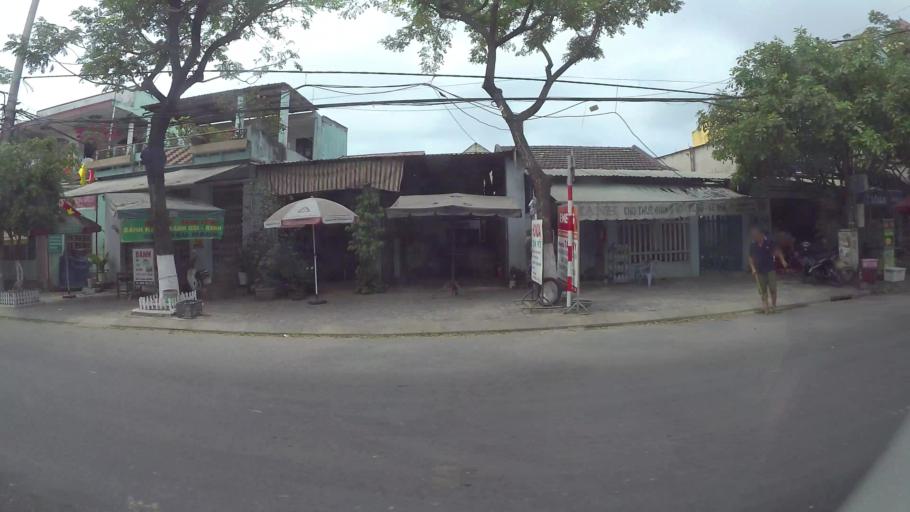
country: VN
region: Da Nang
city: Cam Le
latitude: 16.0360
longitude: 108.1837
